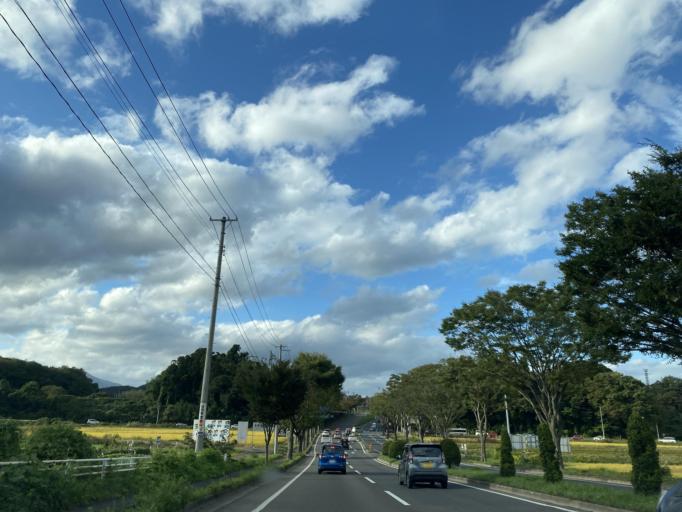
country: JP
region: Miyagi
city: Sendai-shi
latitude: 38.3273
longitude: 140.8422
